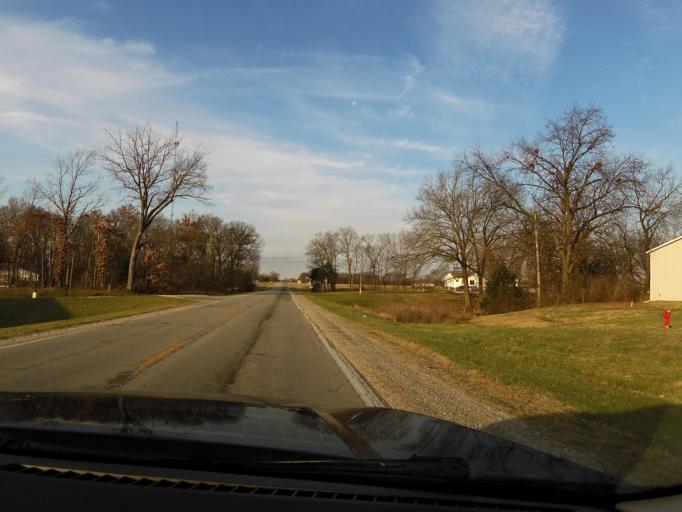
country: US
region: Illinois
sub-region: Bond County
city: Greenville
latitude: 38.9185
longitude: -89.2698
